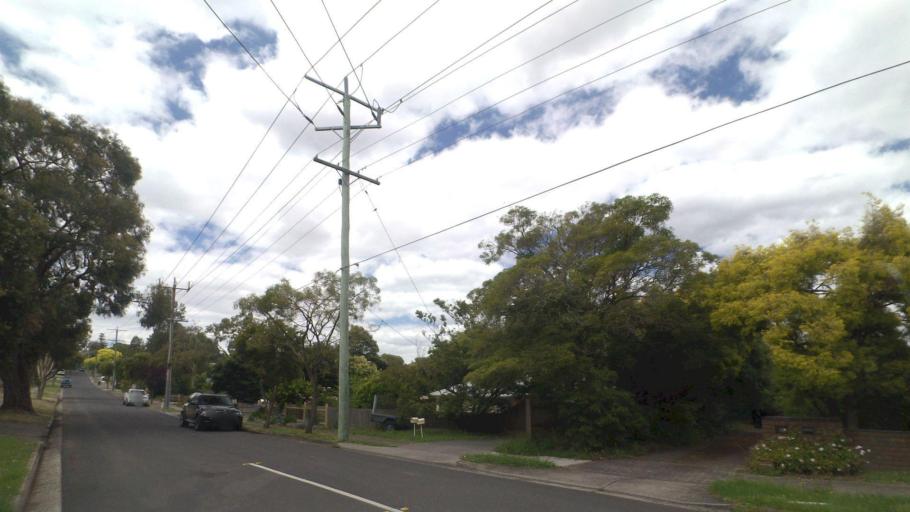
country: AU
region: Victoria
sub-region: Knox
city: Bayswater
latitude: -37.8627
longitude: 145.2632
